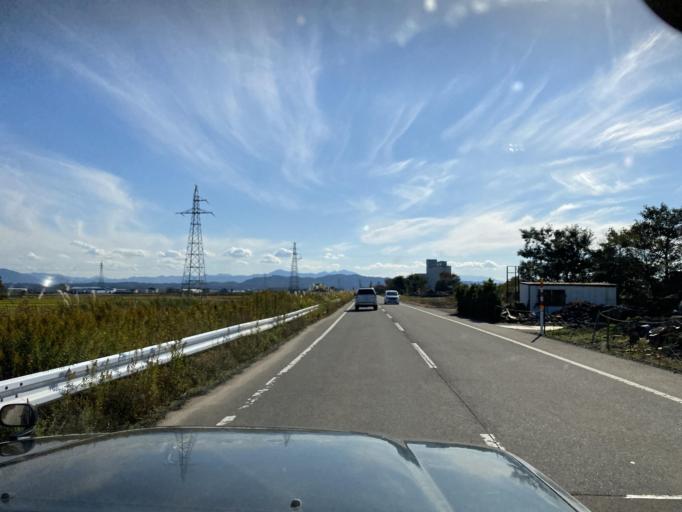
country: JP
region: Niigata
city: Niitsu-honcho
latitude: 37.7987
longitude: 139.0770
